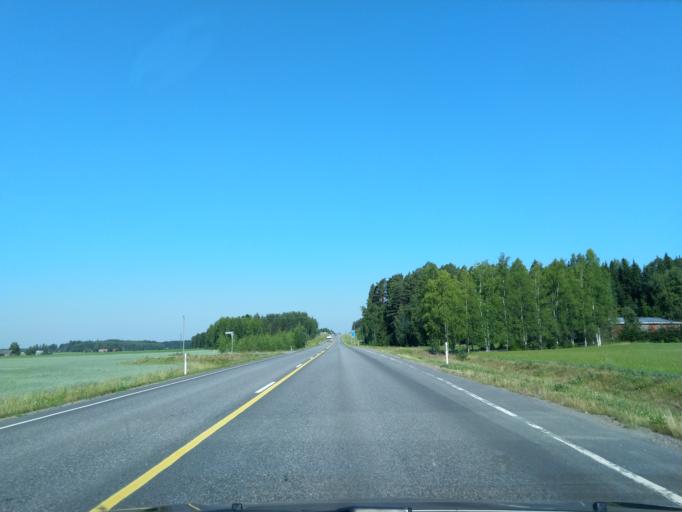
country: FI
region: Varsinais-Suomi
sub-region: Loimaa
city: Alastaro
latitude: 61.0465
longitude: 22.9758
